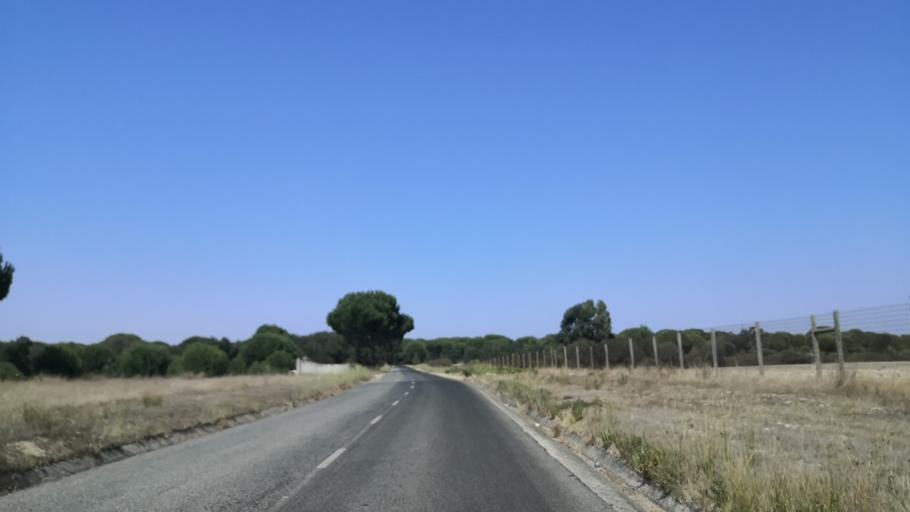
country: PT
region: Santarem
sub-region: Benavente
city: Poceirao
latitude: 38.7313
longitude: -8.7014
